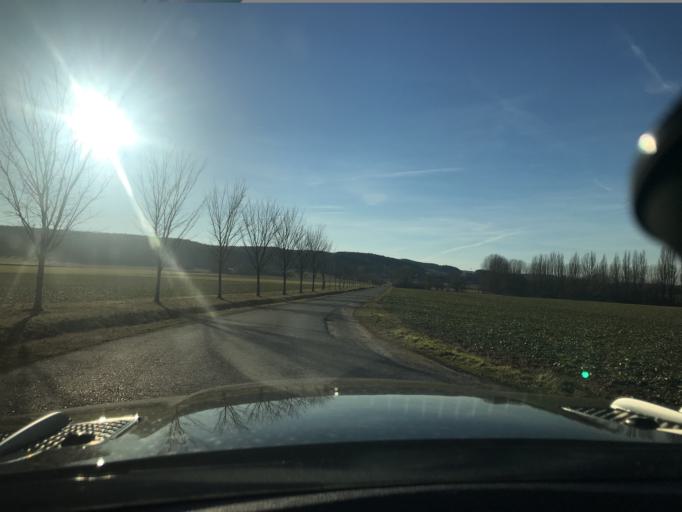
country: DE
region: Thuringia
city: Hausen
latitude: 51.3633
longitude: 10.3568
